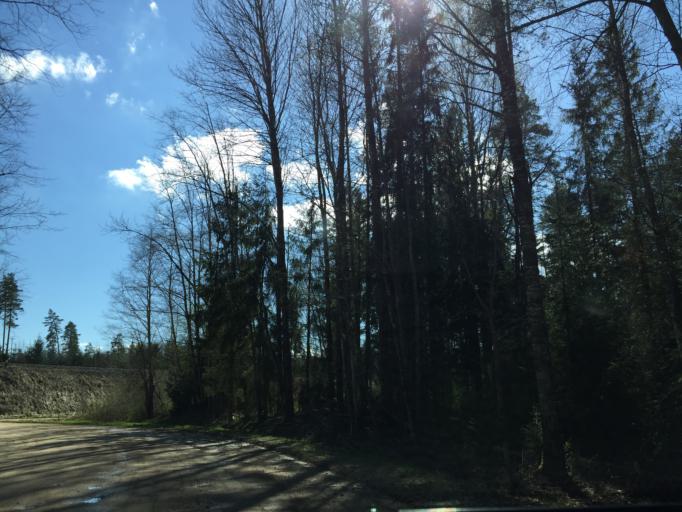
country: EE
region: Valgamaa
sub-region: Valga linn
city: Valga
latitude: 57.8488
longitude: 26.1669
